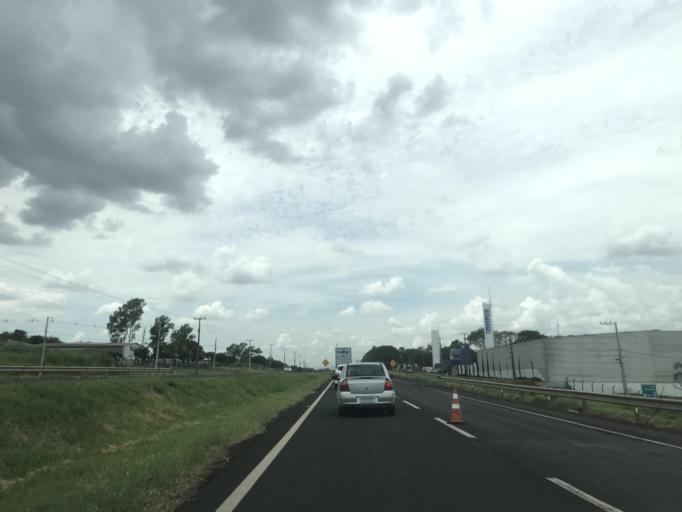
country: BR
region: Parana
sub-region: Mandaguacu
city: Mandaguacu
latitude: -23.3822
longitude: -52.0336
